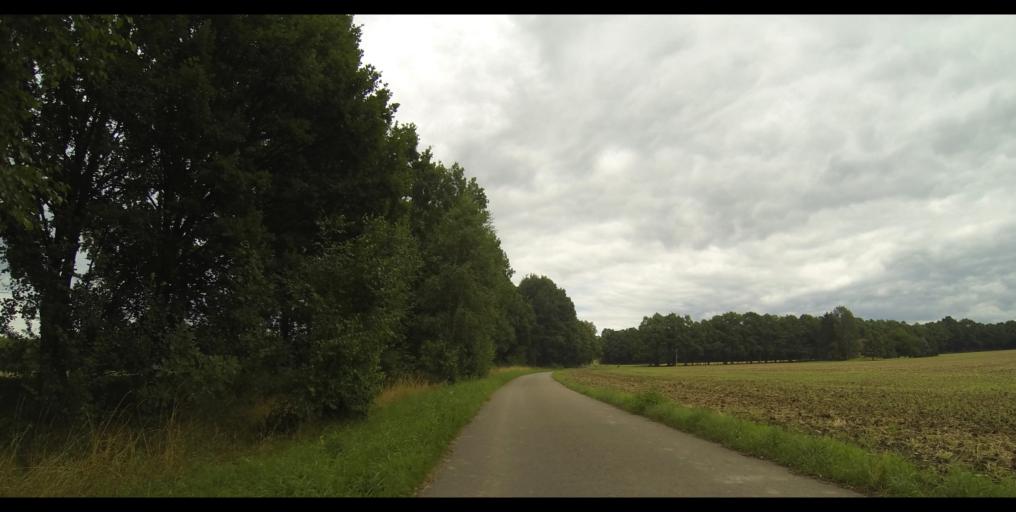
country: DE
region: Saxony
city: Wilsdruff
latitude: 51.0479
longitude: 13.4957
